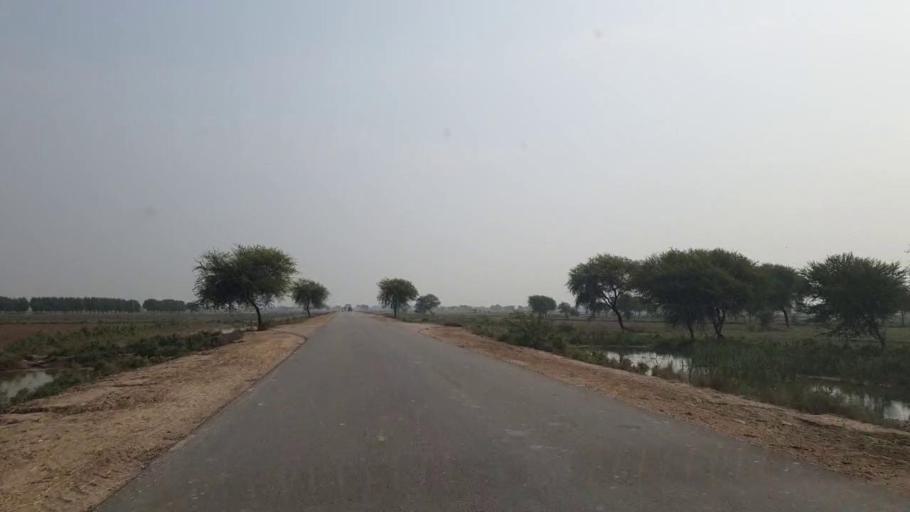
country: PK
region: Sindh
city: Matli
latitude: 25.0605
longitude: 68.6679
